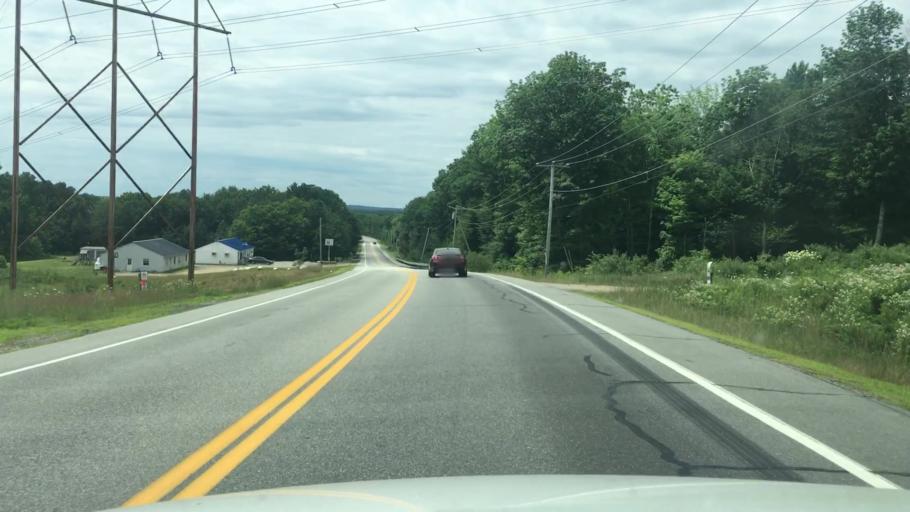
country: US
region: Maine
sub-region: Waldo County
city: Palermo
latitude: 44.4103
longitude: -69.5284
